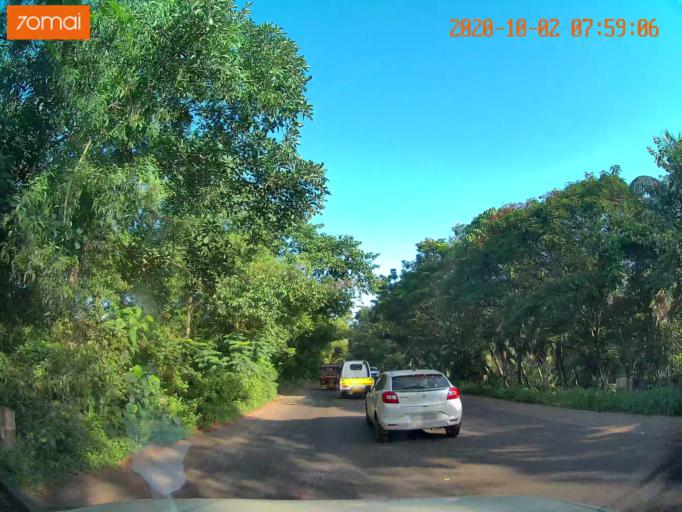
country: IN
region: Kerala
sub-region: Kozhikode
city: Ferokh
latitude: 11.2078
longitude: 75.8630
